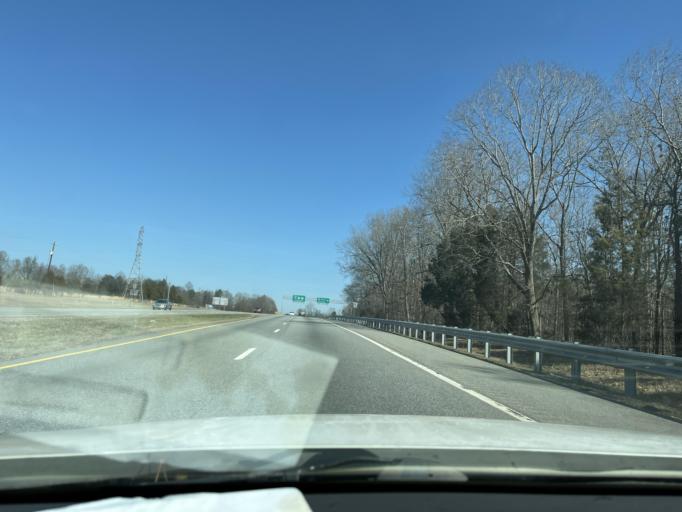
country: US
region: North Carolina
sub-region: Guilford County
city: Jamestown
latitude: 35.9838
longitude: -79.8919
